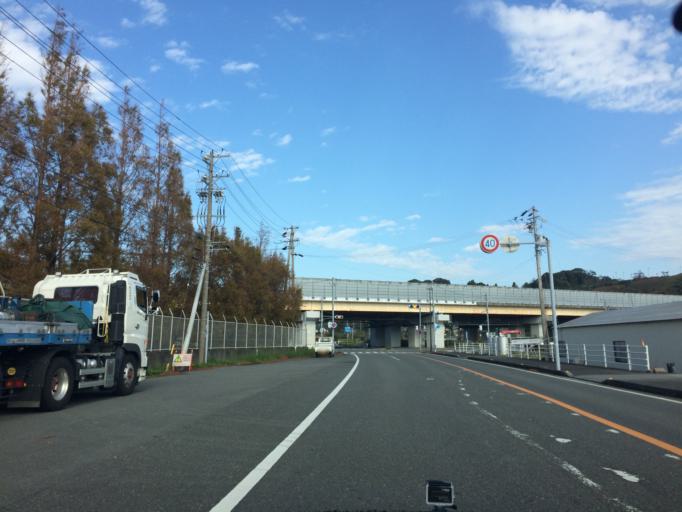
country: JP
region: Shizuoka
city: Shimada
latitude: 34.7747
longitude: 138.2287
